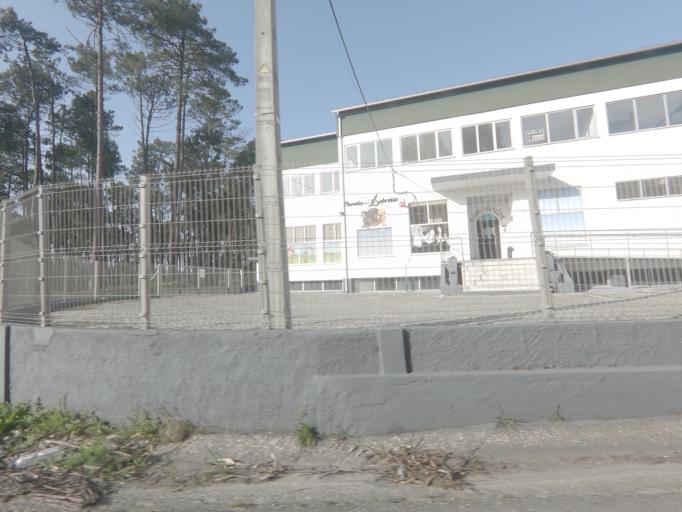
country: PT
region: Leiria
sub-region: Marinha Grande
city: Marinha Grande
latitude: 39.7477
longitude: -8.9057
